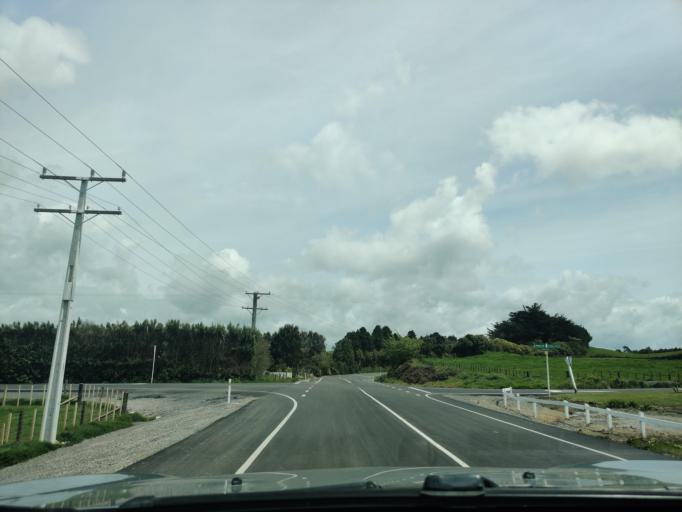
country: NZ
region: Taranaki
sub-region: South Taranaki District
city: Eltham
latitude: -39.3769
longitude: 174.1729
